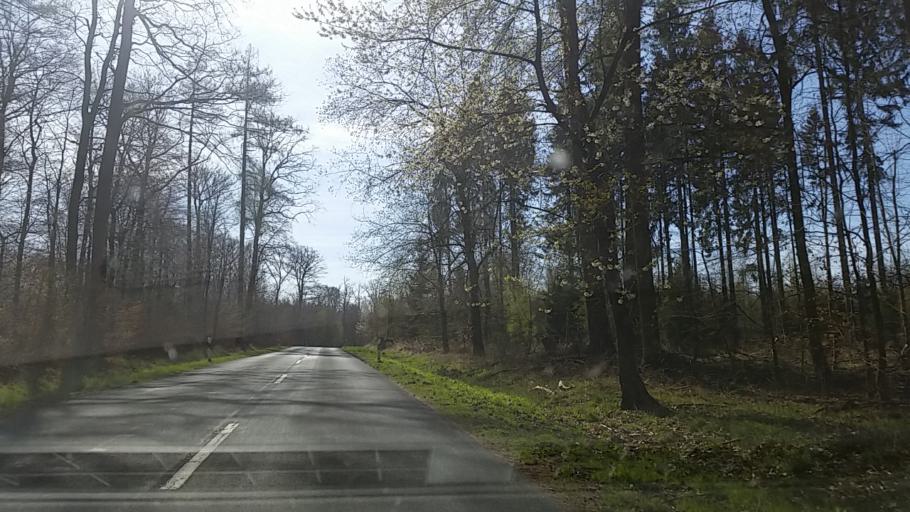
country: DE
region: Lower Saxony
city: Rabke
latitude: 52.1771
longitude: 10.8549
